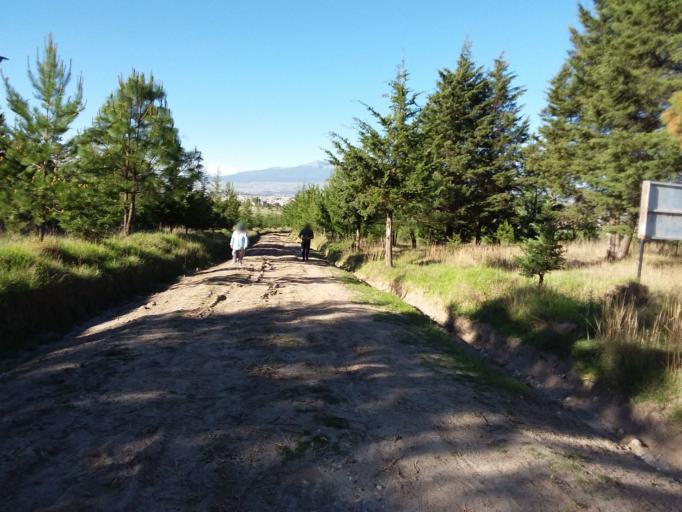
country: MX
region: Mexico
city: San Marcos Yachihuacaltepec
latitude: 19.3131
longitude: -99.6955
